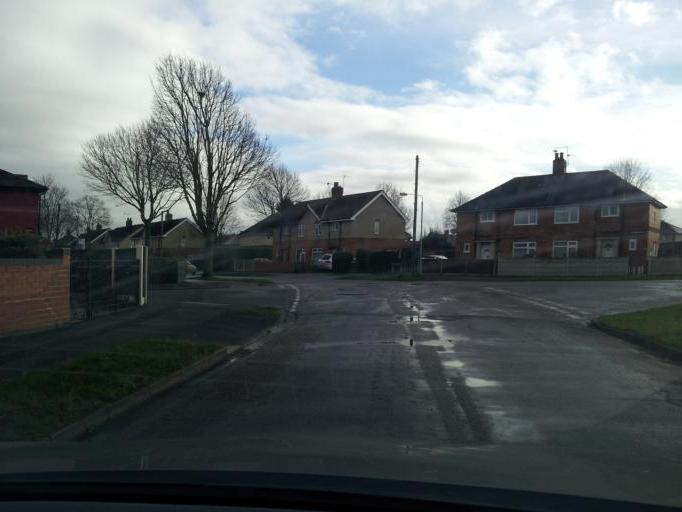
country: GB
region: England
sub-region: Nottinghamshire
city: Newark on Trent
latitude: 53.0643
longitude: -0.8084
